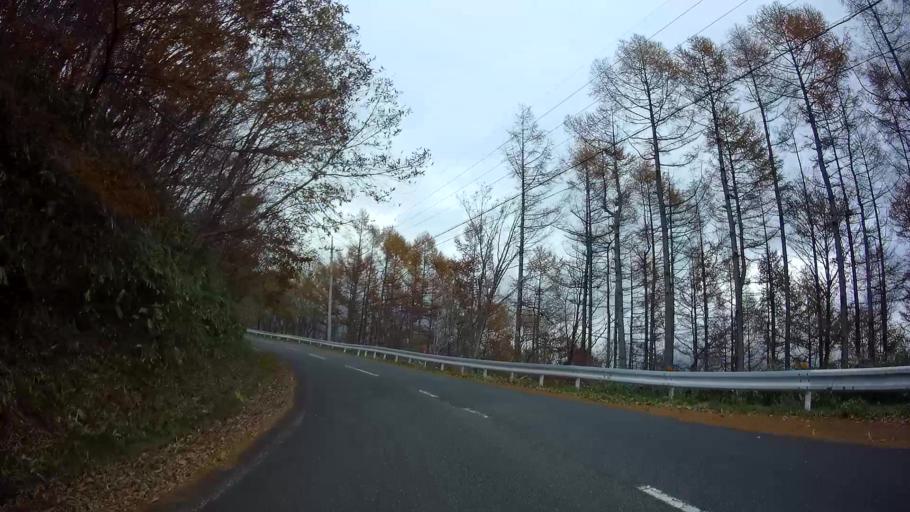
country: JP
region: Gunma
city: Nakanojomachi
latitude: 36.6777
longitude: 138.6637
